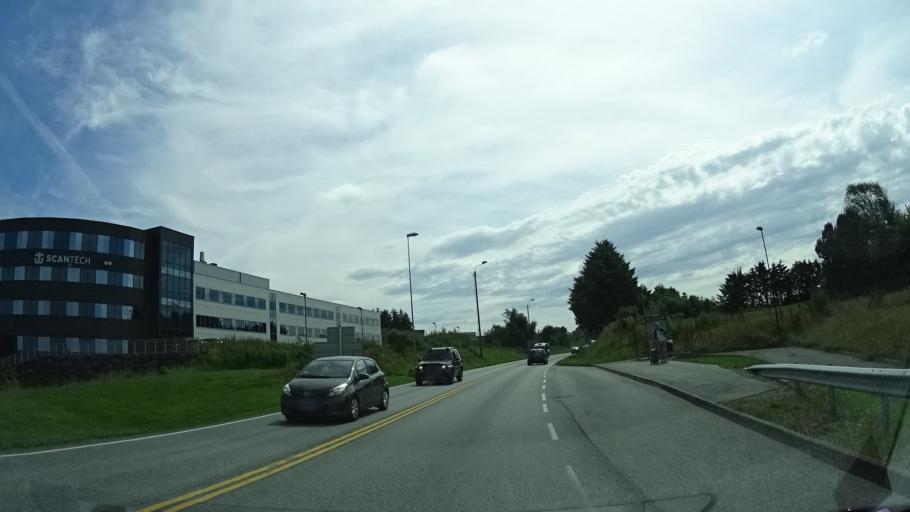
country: NO
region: Rogaland
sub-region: Randaberg
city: Randaberg
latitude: 58.9947
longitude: 5.6512
